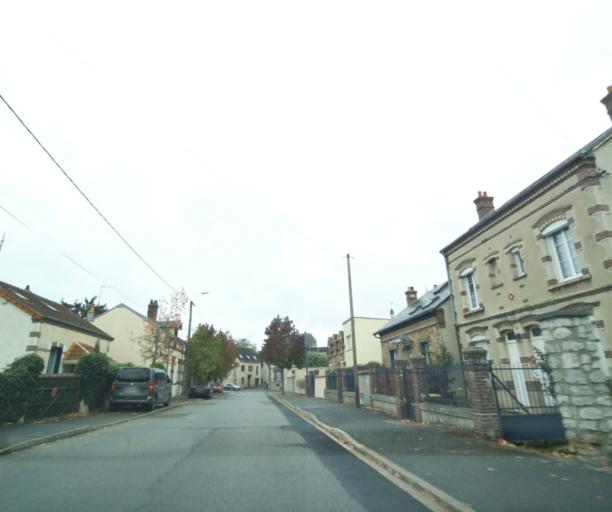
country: FR
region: Centre
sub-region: Departement d'Eure-et-Loir
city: Dreux
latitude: 48.7281
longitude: 1.3677
